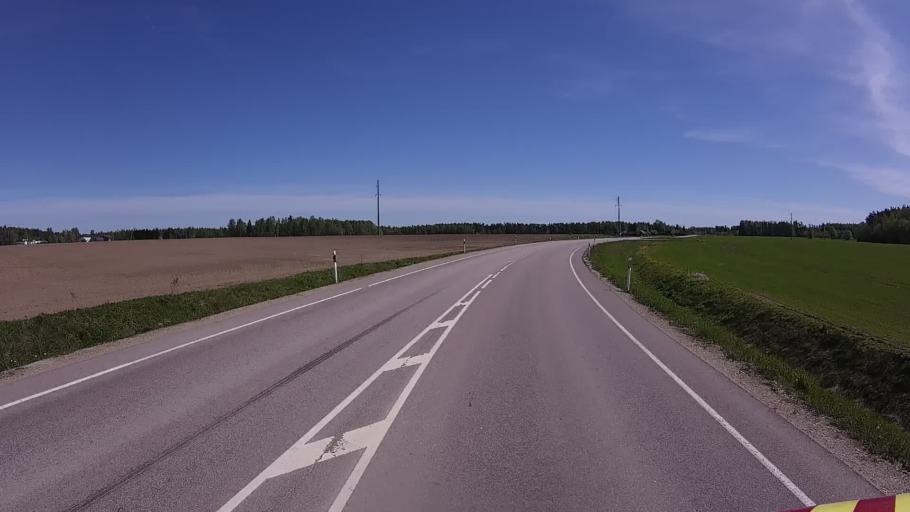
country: EE
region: Polvamaa
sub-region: Polva linn
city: Polva
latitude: 58.0893
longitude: 27.0933
